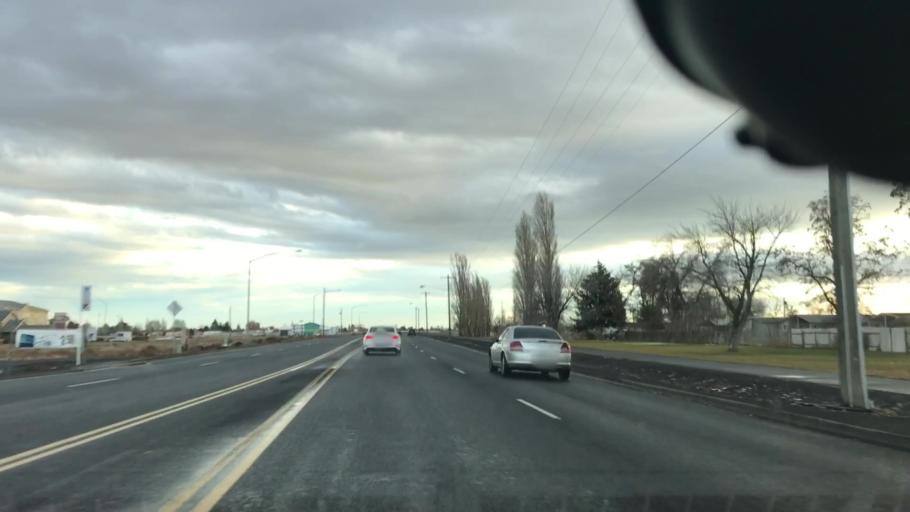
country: US
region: Washington
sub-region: Grant County
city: Moses Lake North
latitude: 47.1634
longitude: -119.3138
